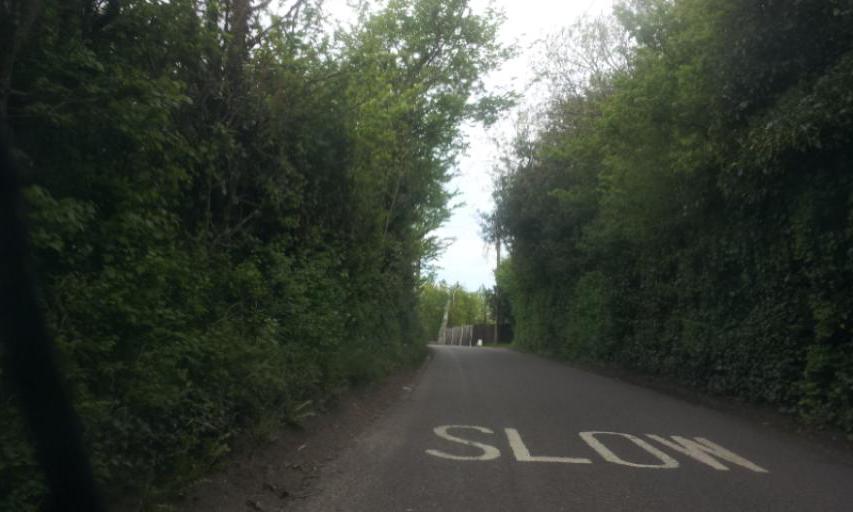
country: GB
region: England
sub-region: Kent
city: Swanley
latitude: 51.3990
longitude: 0.1451
